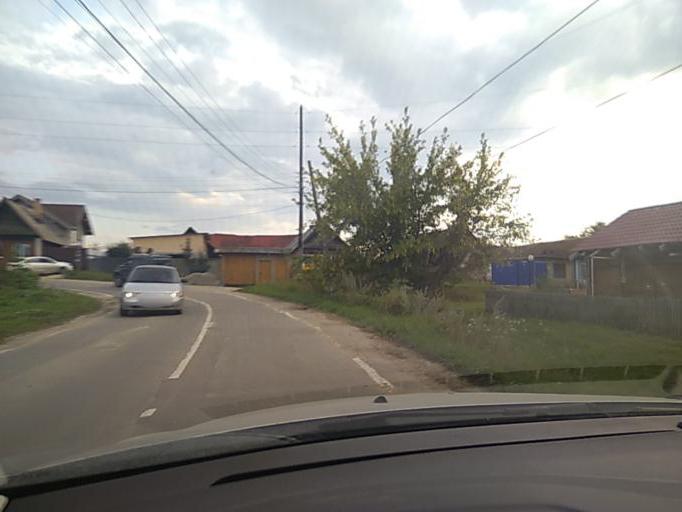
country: RU
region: Chelyabinsk
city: Kyshtym
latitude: 55.6939
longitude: 60.5306
